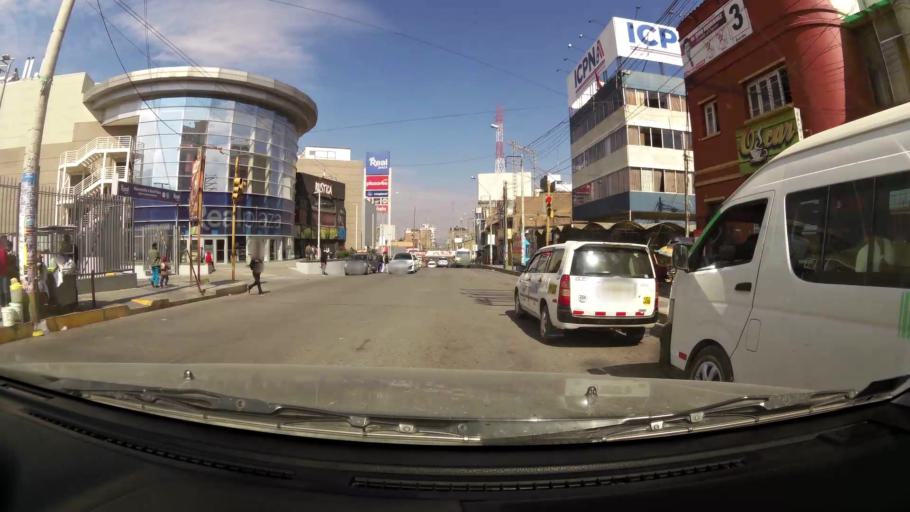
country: PE
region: Junin
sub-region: Provincia de Huancayo
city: Huancayo
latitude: -12.0658
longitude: -75.2050
